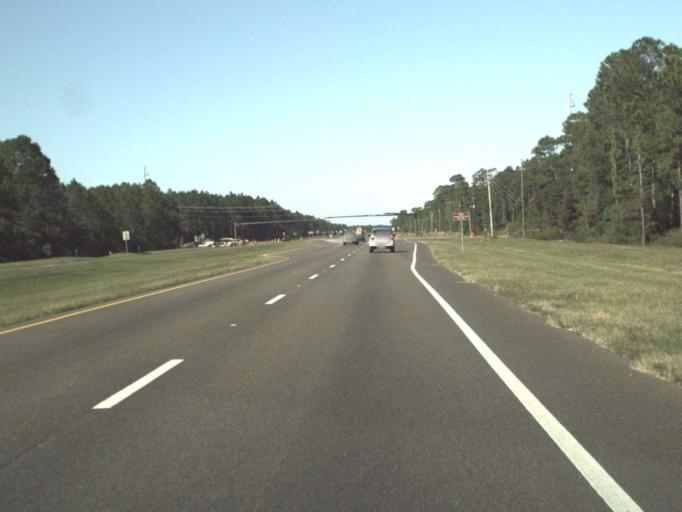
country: US
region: Florida
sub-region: Walton County
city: Seaside
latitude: 30.3572
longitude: -86.1269
